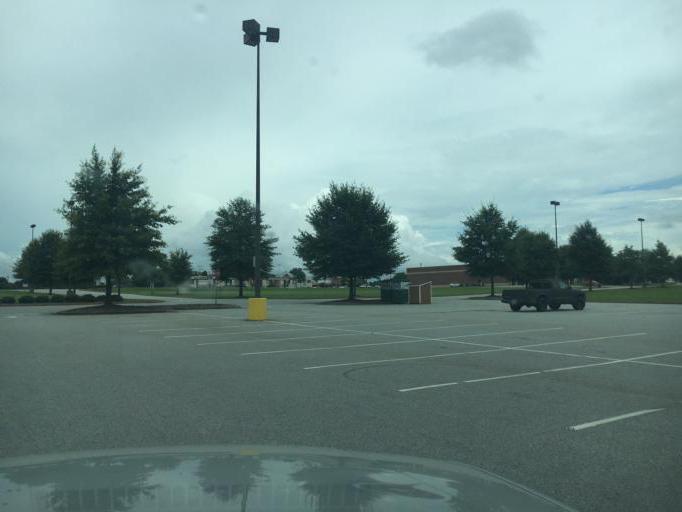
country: US
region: South Carolina
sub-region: Anderson County
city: Centerville
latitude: 34.5095
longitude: -82.7602
